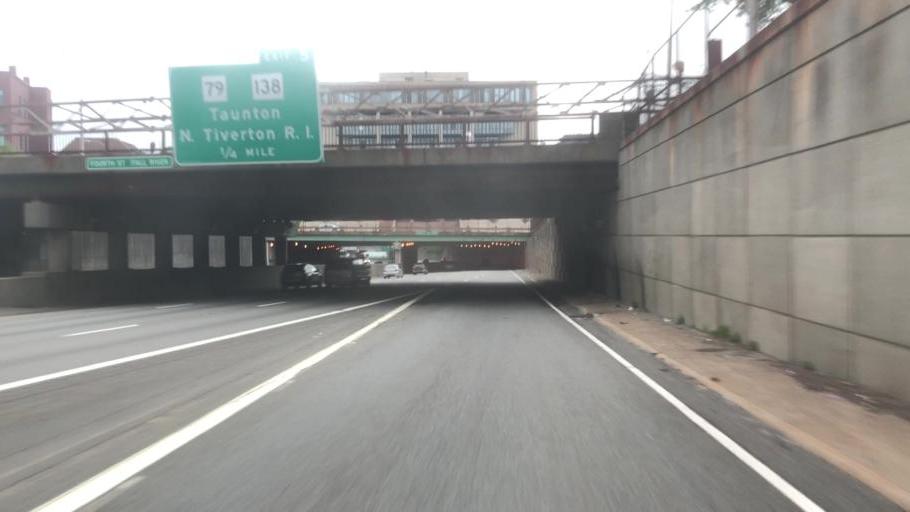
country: US
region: Massachusetts
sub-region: Bristol County
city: Fall River
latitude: 41.6996
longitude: -71.1528
